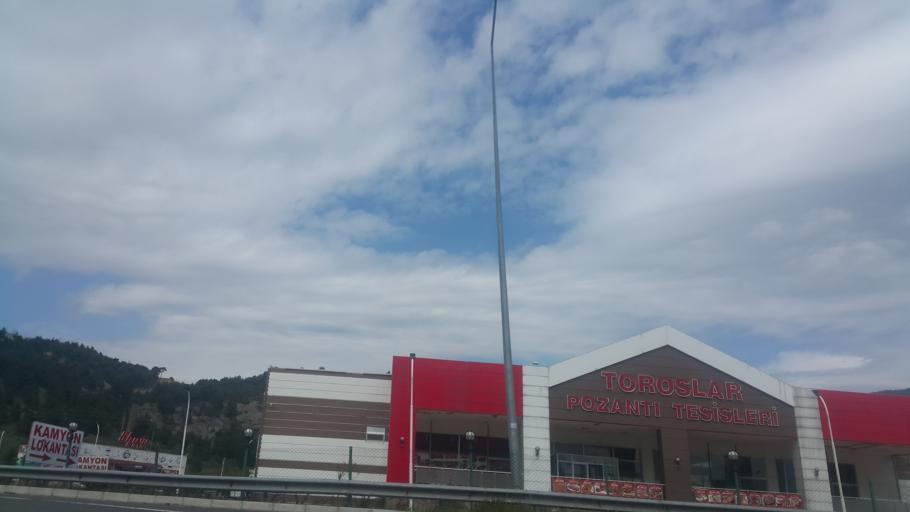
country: TR
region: Adana
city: Pozanti
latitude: 37.4612
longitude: 34.8776
